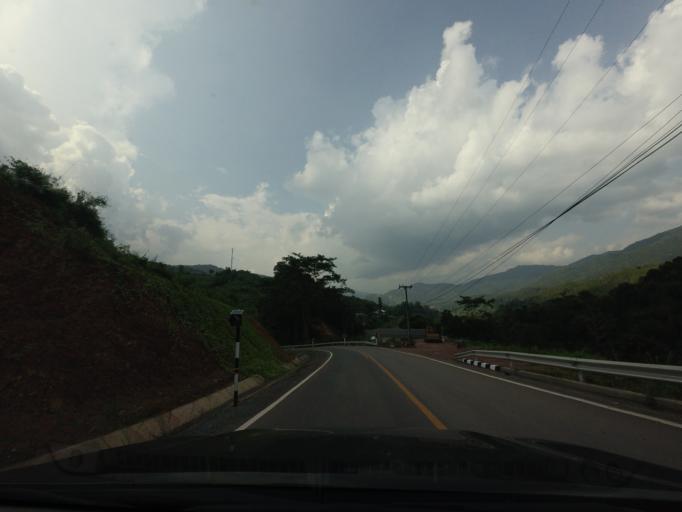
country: TH
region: Nan
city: Bo Kluea
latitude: 19.2053
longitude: 101.1859
